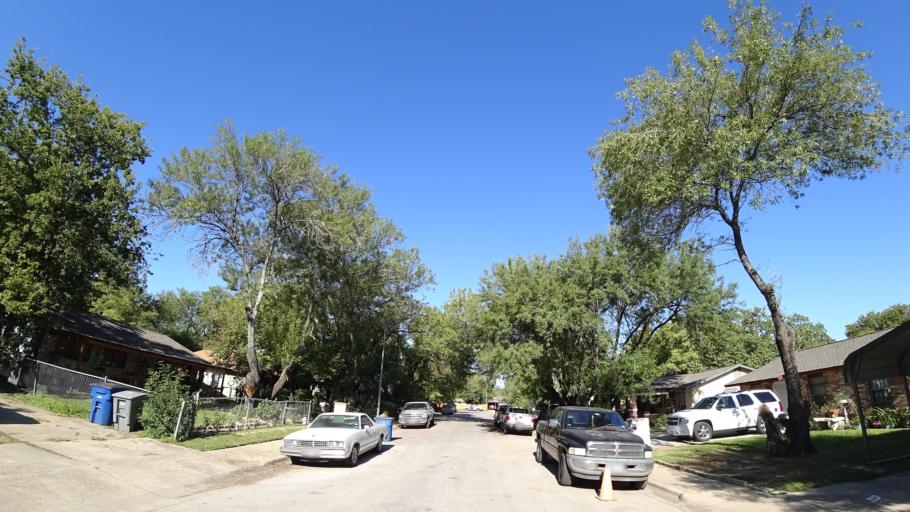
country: US
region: Texas
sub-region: Travis County
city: Austin
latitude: 30.2309
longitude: -97.6927
